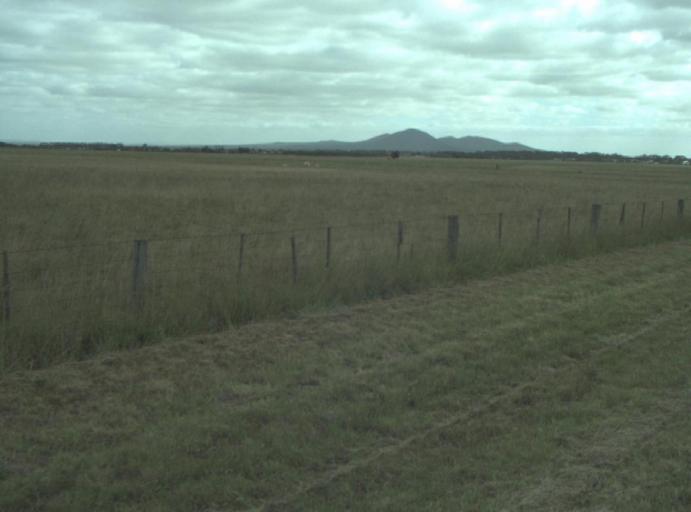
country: AU
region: Victoria
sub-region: Greater Geelong
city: Lara
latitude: -38.0502
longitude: 144.3986
